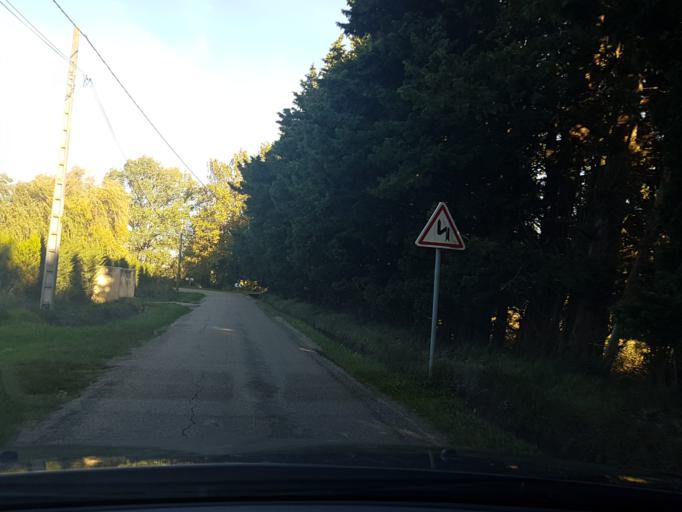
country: FR
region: Provence-Alpes-Cote d'Azur
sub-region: Departement du Vaucluse
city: Althen-des-Paluds
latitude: 44.0338
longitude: 4.9628
